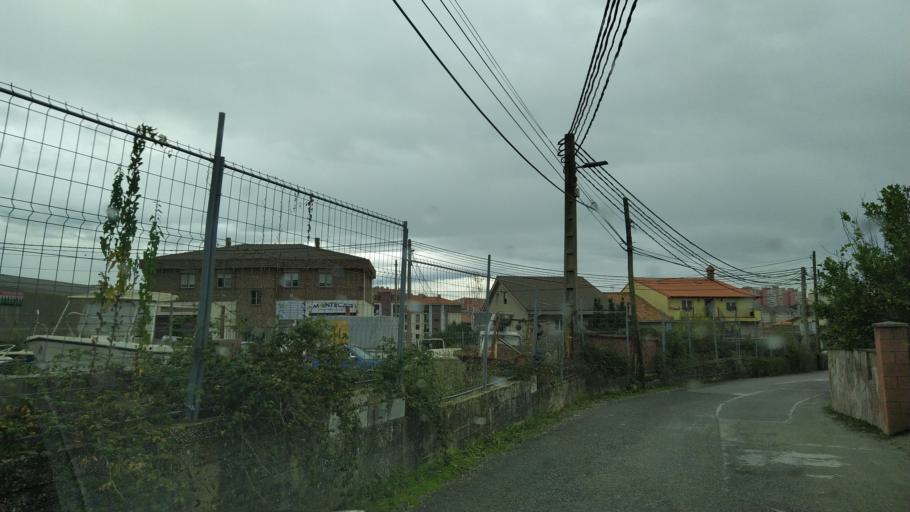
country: ES
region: Cantabria
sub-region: Provincia de Cantabria
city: Santander
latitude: 43.4718
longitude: -3.8245
